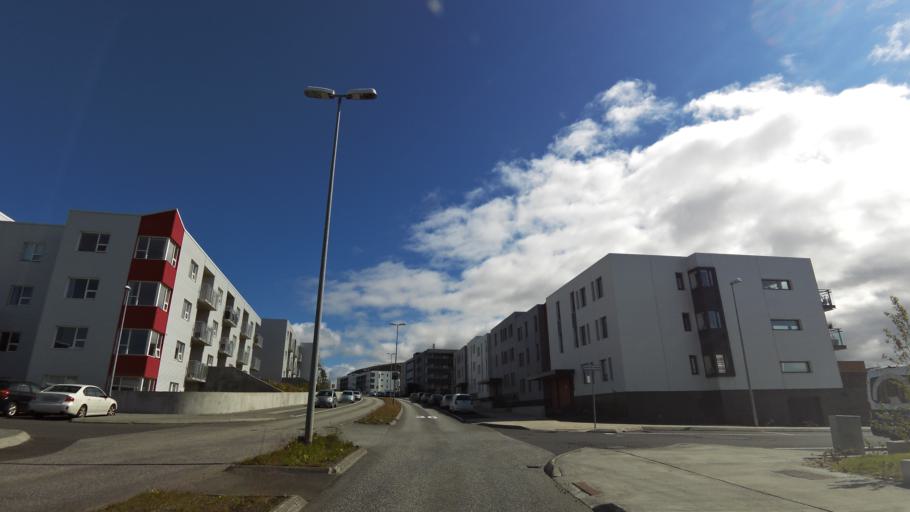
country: IS
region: Capital Region
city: Mosfellsbaer
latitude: 64.1681
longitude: -21.6693
